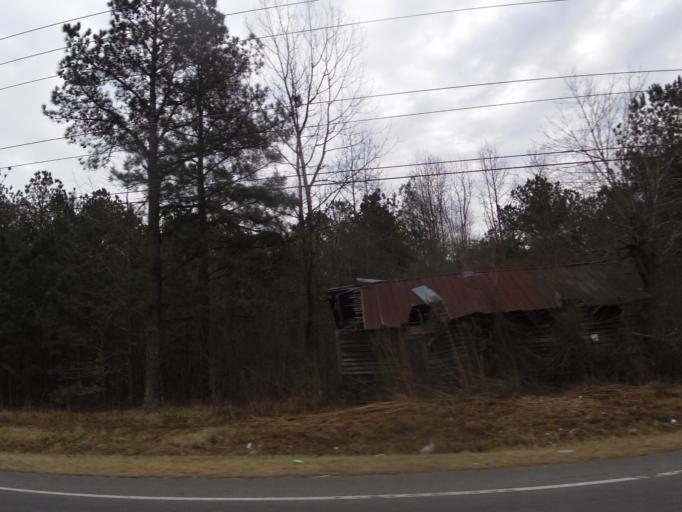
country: US
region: North Carolina
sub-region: Northampton County
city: Jackson
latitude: 36.2833
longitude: -77.2784
